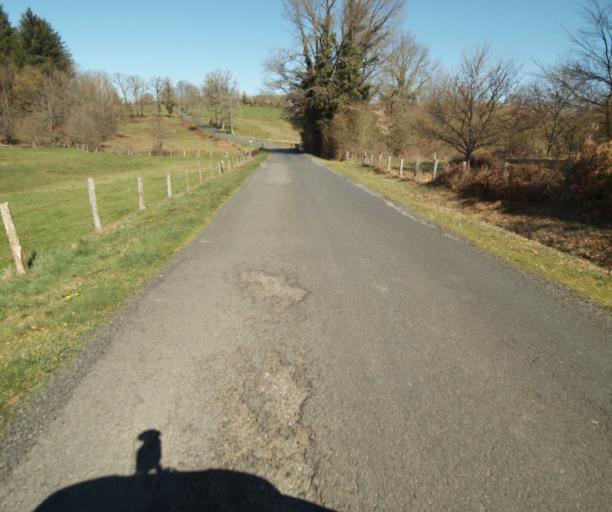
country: FR
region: Limousin
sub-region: Departement de la Correze
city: Saint-Clement
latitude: 45.3313
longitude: 1.6568
